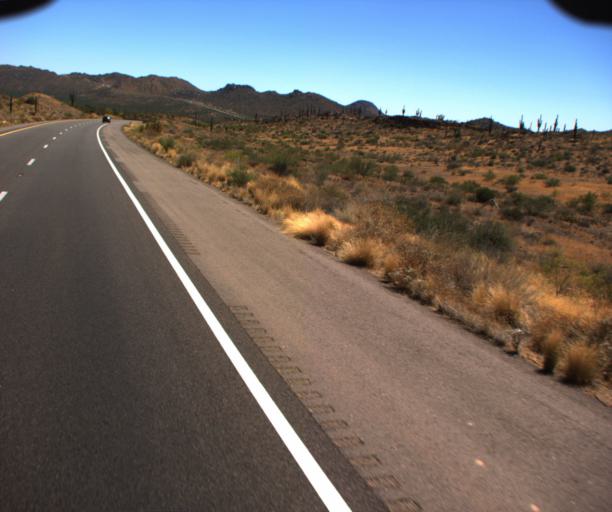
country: US
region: Arizona
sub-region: Maricopa County
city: Rio Verde
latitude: 33.7426
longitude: -111.5040
